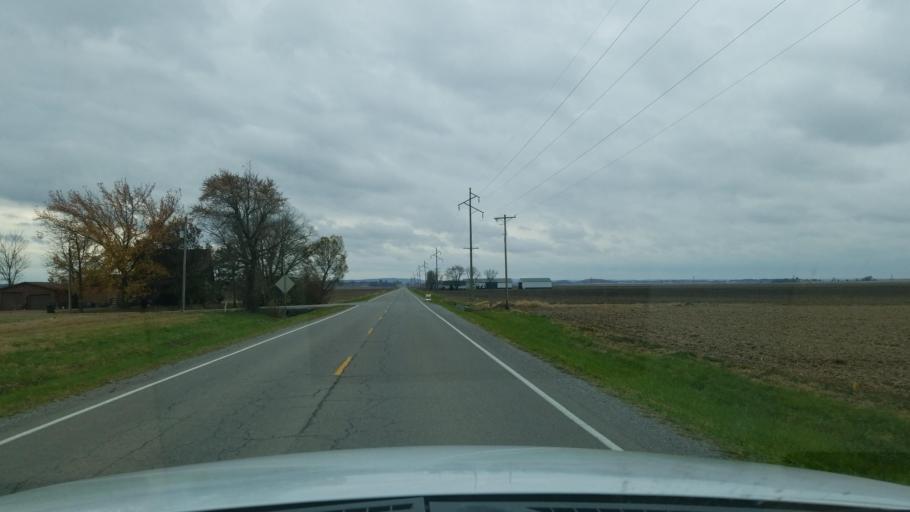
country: US
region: Illinois
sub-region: Saline County
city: Eldorado
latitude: 37.7875
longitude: -88.4382
